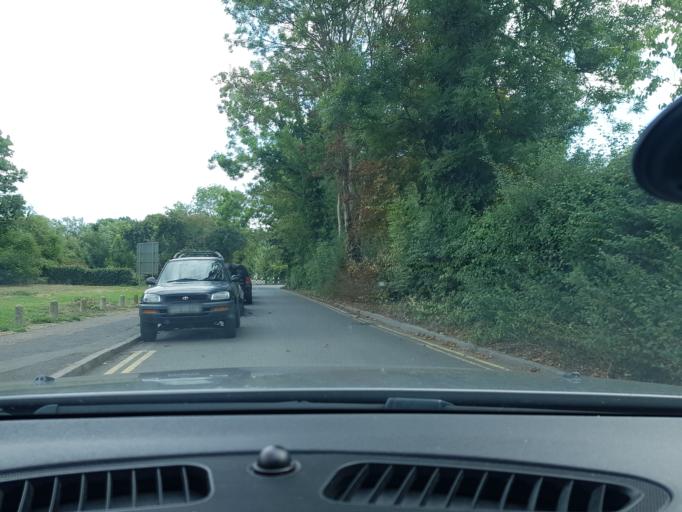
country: GB
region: England
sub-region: Buckinghamshire
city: Iver
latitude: 51.4900
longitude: -0.4859
